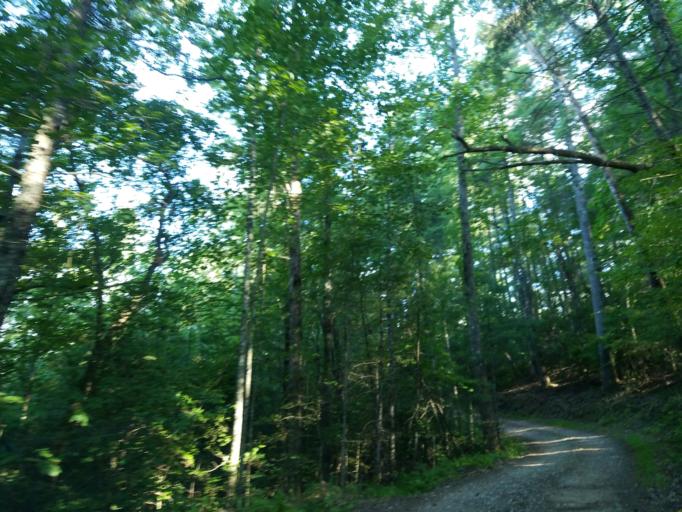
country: US
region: Georgia
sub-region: Union County
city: Blairsville
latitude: 34.7598
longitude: -84.1178
